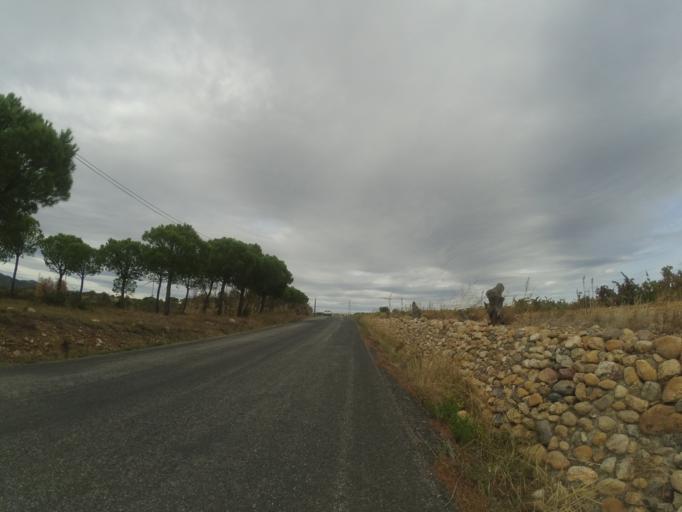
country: FR
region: Languedoc-Roussillon
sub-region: Departement des Pyrenees-Orientales
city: Pezilla-la-Riviere
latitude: 42.7100
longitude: 2.7592
